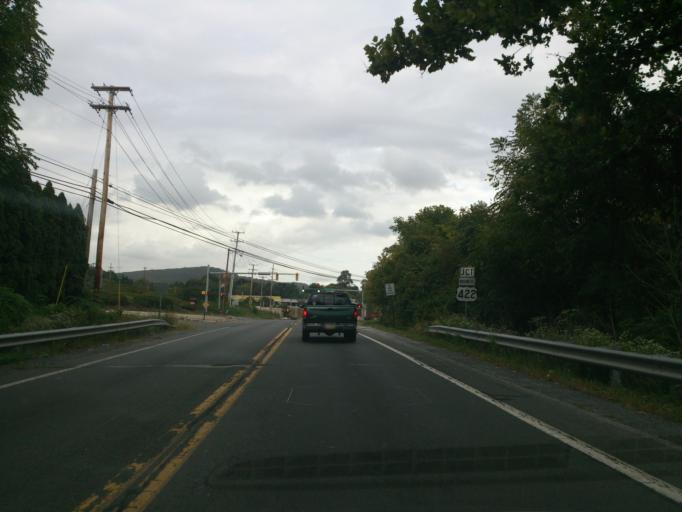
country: US
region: Pennsylvania
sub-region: Berks County
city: Reiffton
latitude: 40.3109
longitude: -75.8711
